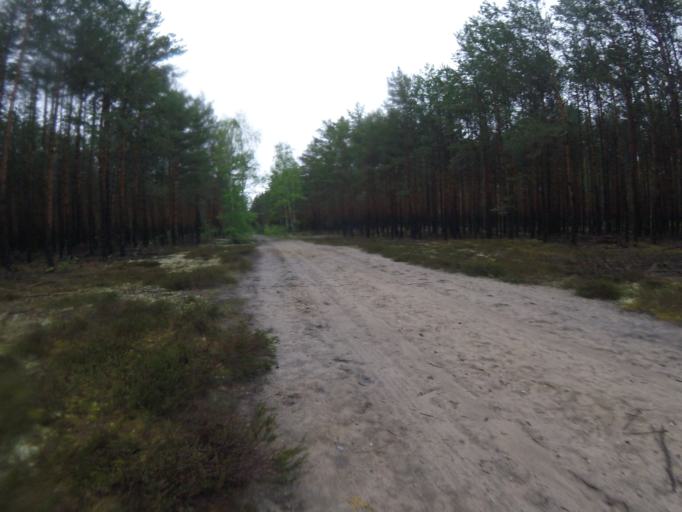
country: DE
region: Brandenburg
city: Schwerin
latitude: 52.1346
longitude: 13.6352
